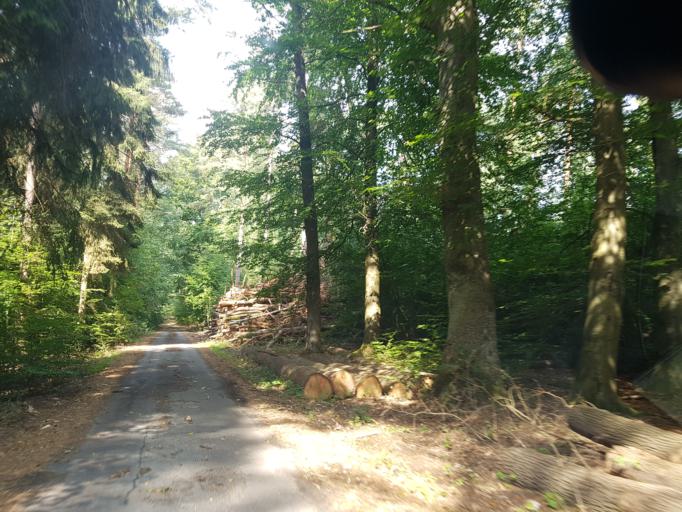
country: DE
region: Brandenburg
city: Gorzke
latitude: 52.0619
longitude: 12.2713
